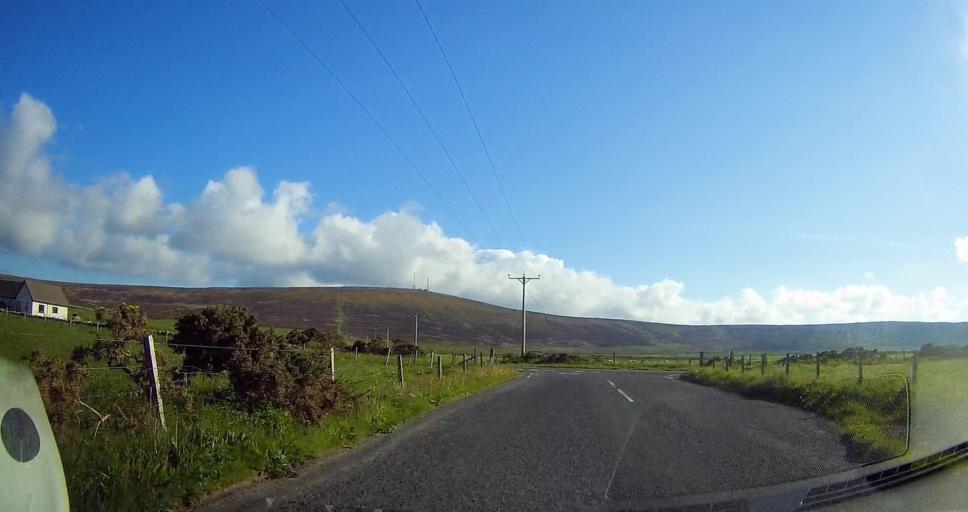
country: GB
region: Scotland
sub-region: Orkney Islands
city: Orkney
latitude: 58.9926
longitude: -3.0726
